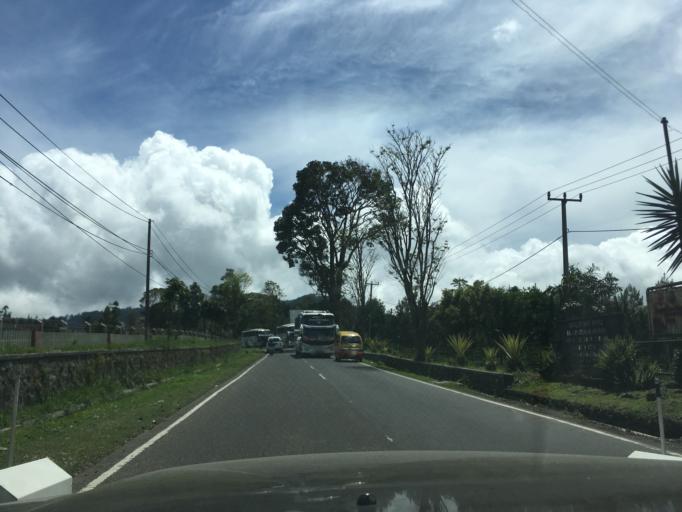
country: ID
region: West Java
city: Lembang
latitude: -6.8004
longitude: 107.6512
